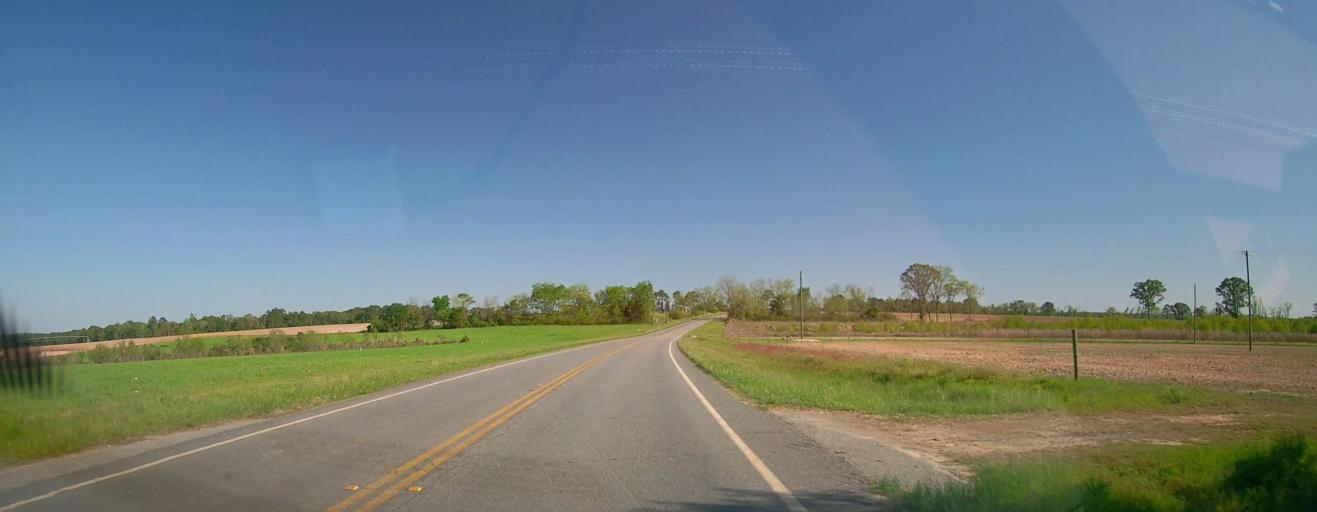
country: US
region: Georgia
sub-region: Wilcox County
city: Rochelle
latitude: 31.9832
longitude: -83.4589
